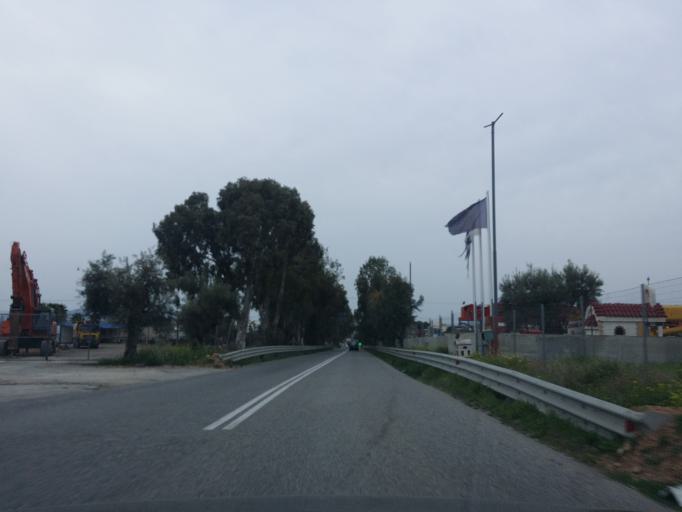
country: GR
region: Attica
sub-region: Nomarchia Dytikis Attikis
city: Mandra
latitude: 38.0830
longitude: 23.4918
